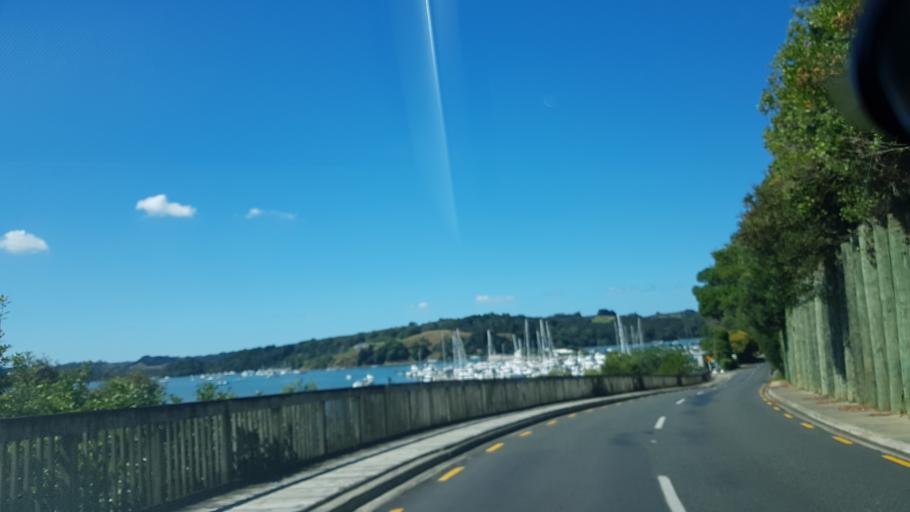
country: NZ
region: Auckland
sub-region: Auckland
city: Warkworth
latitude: -36.3924
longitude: 174.7227
